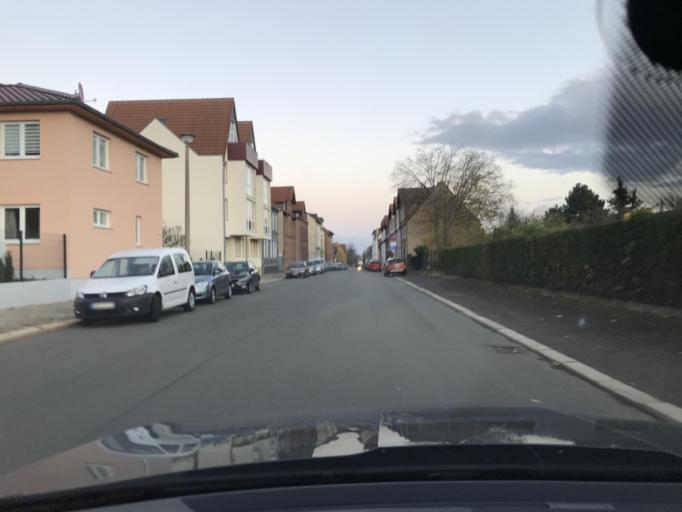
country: DE
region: Saxony-Anhalt
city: Halberstadt
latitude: 51.8873
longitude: 11.0452
